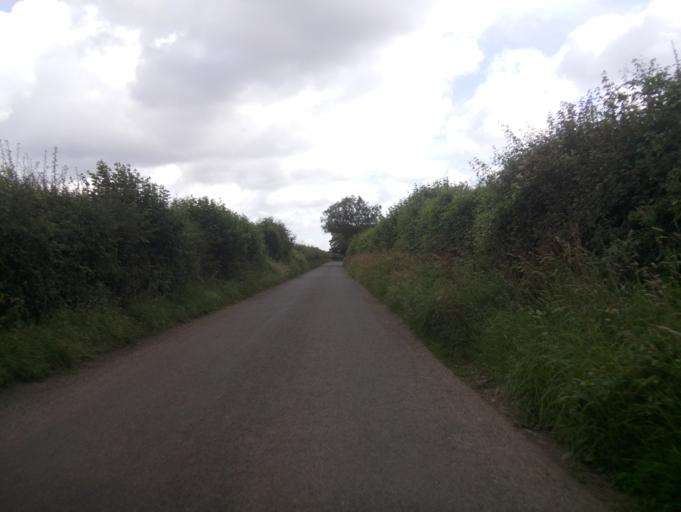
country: GB
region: England
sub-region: Gloucestershire
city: Chalford
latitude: 51.7630
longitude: -2.0877
